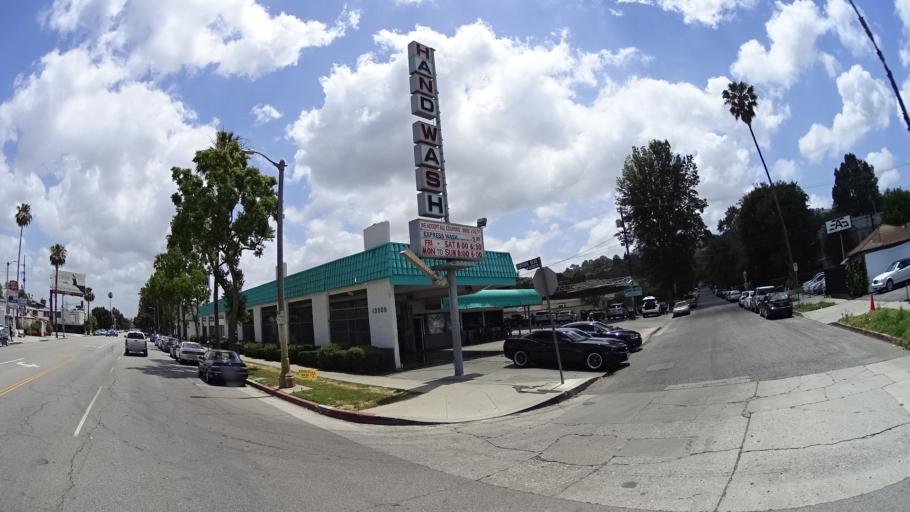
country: US
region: California
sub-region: Los Angeles County
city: Sherman Oaks
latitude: 34.1467
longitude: -118.4236
